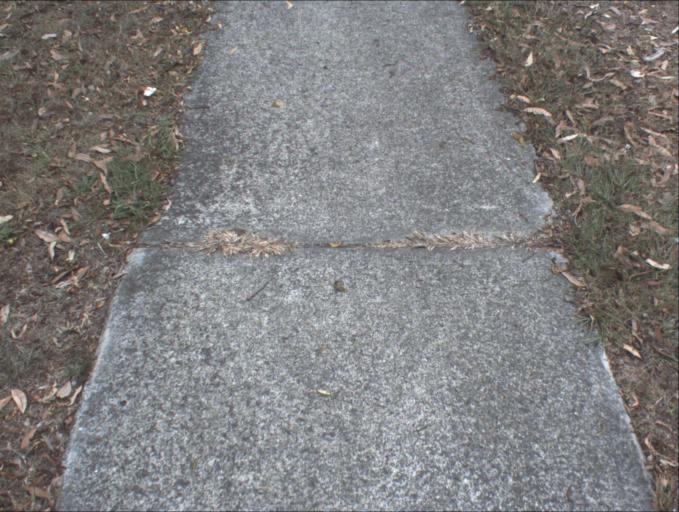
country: AU
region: Queensland
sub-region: Logan
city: Slacks Creek
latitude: -27.6661
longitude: 153.1800
